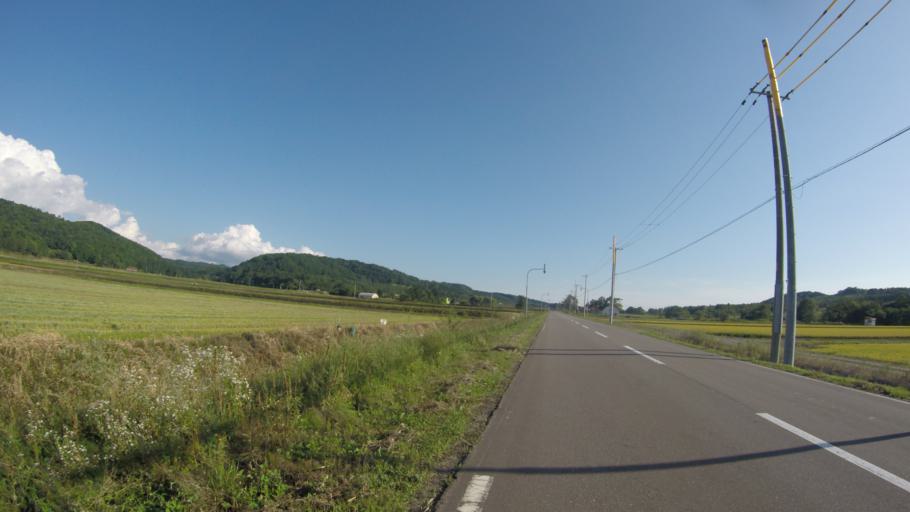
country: JP
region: Hokkaido
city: Iwamizawa
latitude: 43.1958
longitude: 141.8245
